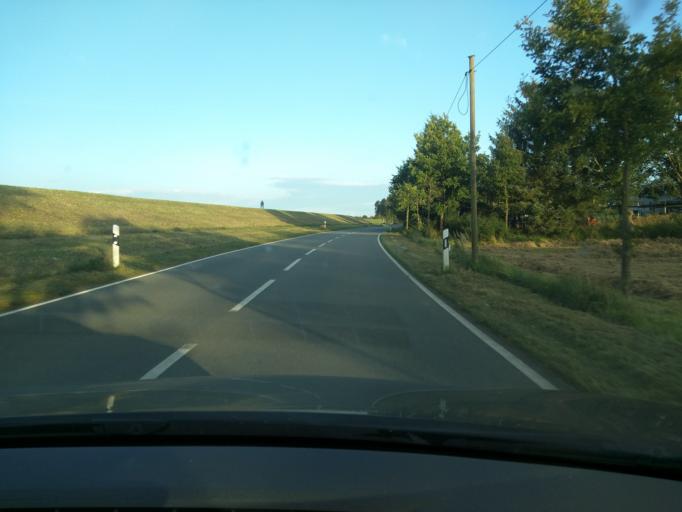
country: DE
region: Lower Saxony
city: Artlenburg
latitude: 53.3788
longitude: 10.4725
